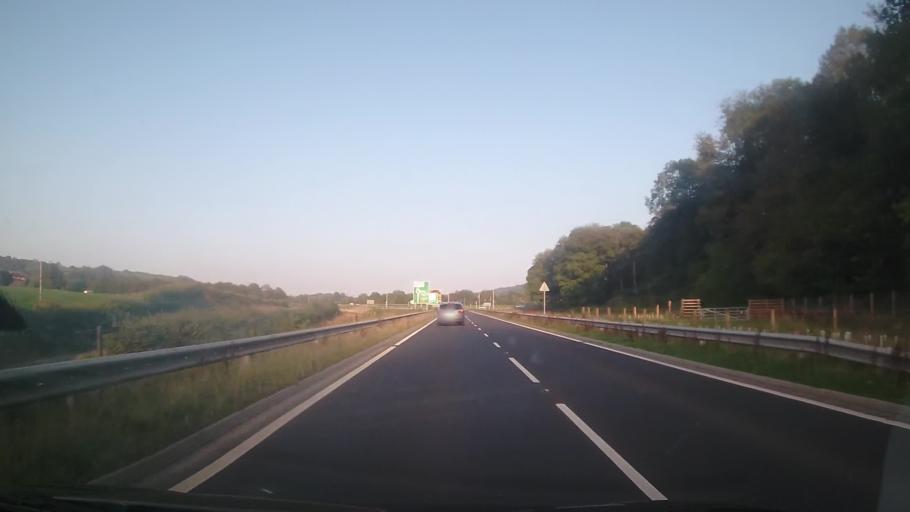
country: GB
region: Wales
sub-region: Sir Powys
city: Mochdre
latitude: 52.5013
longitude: -3.3549
